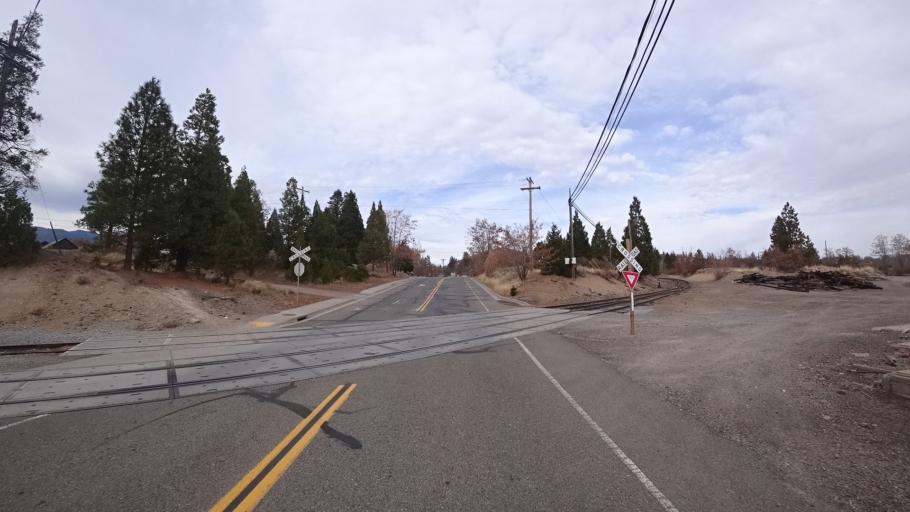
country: US
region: California
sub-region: Siskiyou County
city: Weed
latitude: 41.4280
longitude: -122.3866
